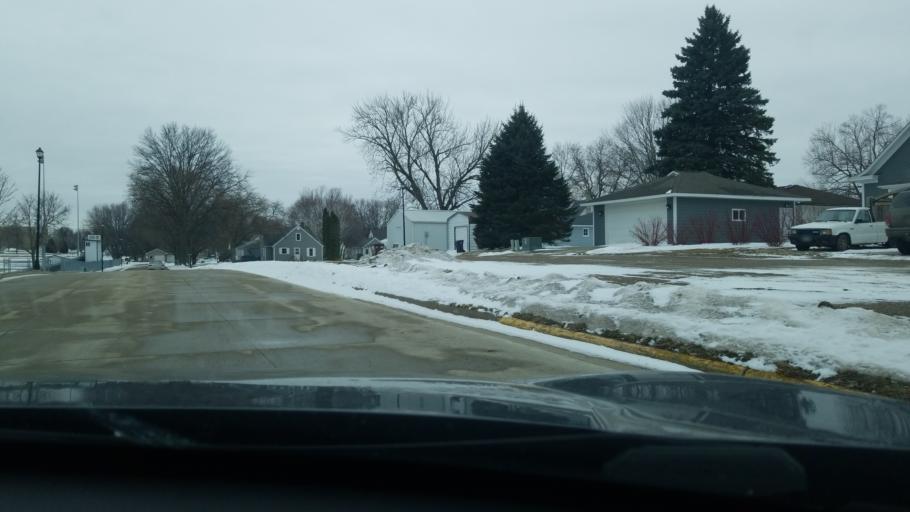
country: US
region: Iowa
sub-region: Lyon County
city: Rock Rapids
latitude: 43.4251
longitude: -96.1700
